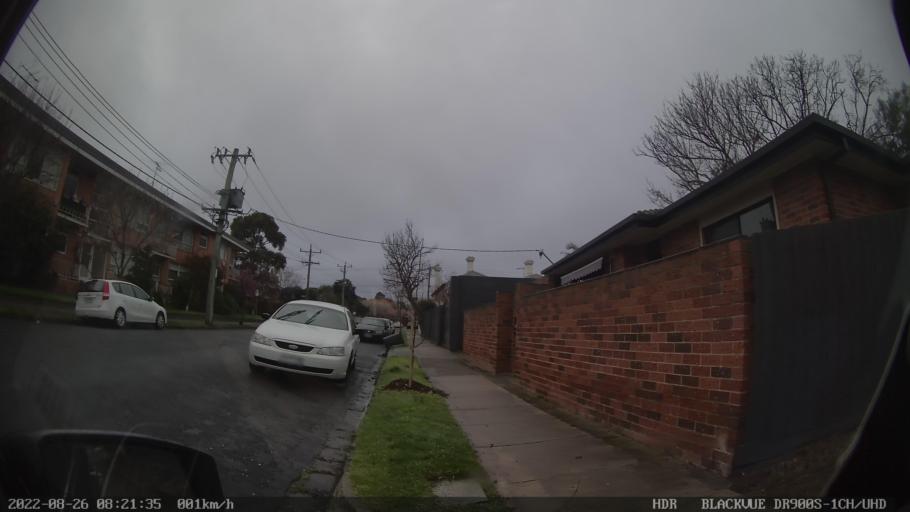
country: AU
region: Victoria
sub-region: Glen Eira
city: Elsternwick
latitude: -37.8870
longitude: 145.0051
